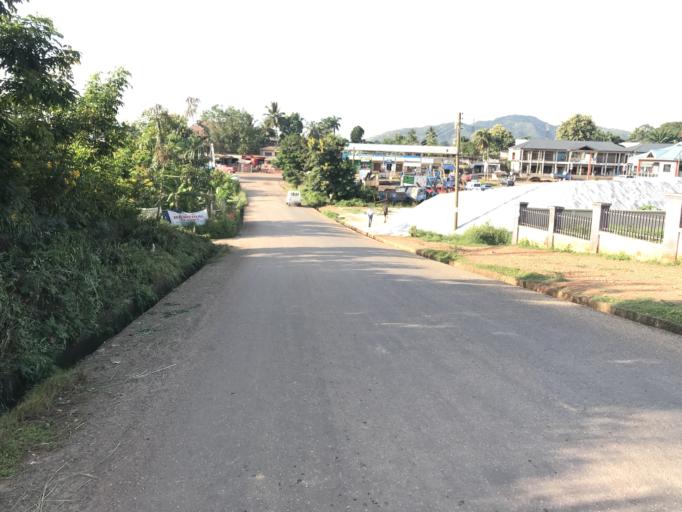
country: GH
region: Ashanti
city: Obuasi
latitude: 6.2048
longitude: -1.6827
